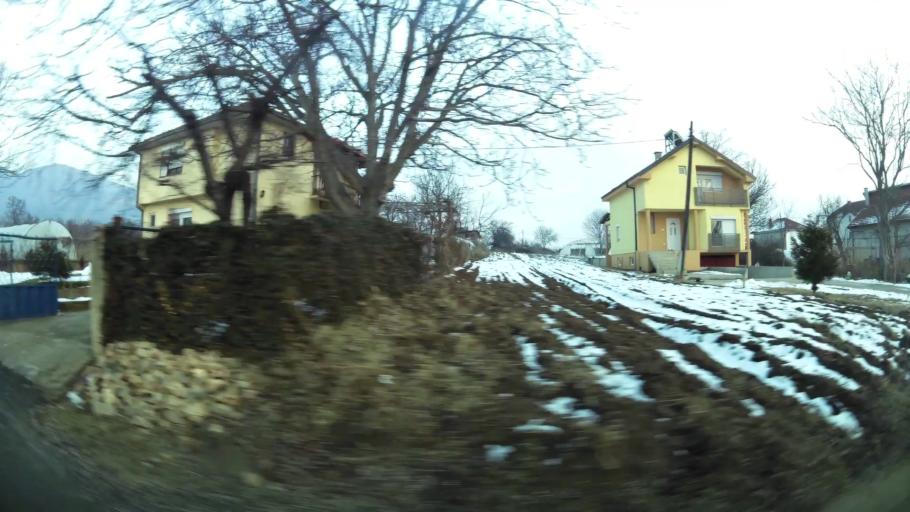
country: MK
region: Aracinovo
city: Arachinovo
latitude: 42.0307
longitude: 21.5461
